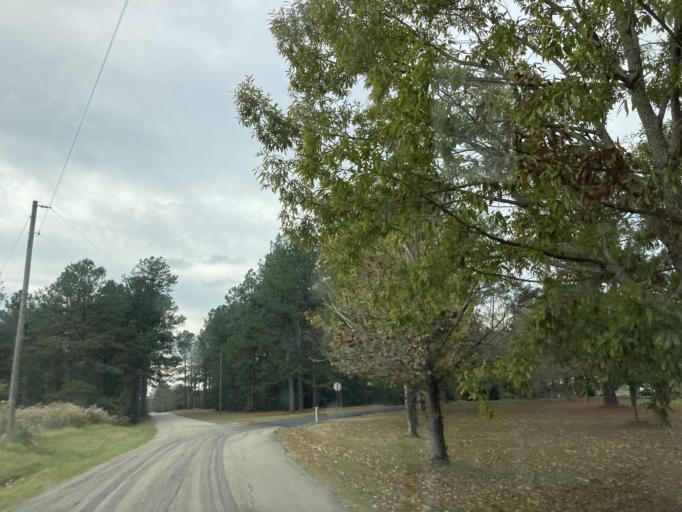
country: US
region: Mississippi
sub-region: Lamar County
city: Purvis
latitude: 31.1435
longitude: -89.4608
